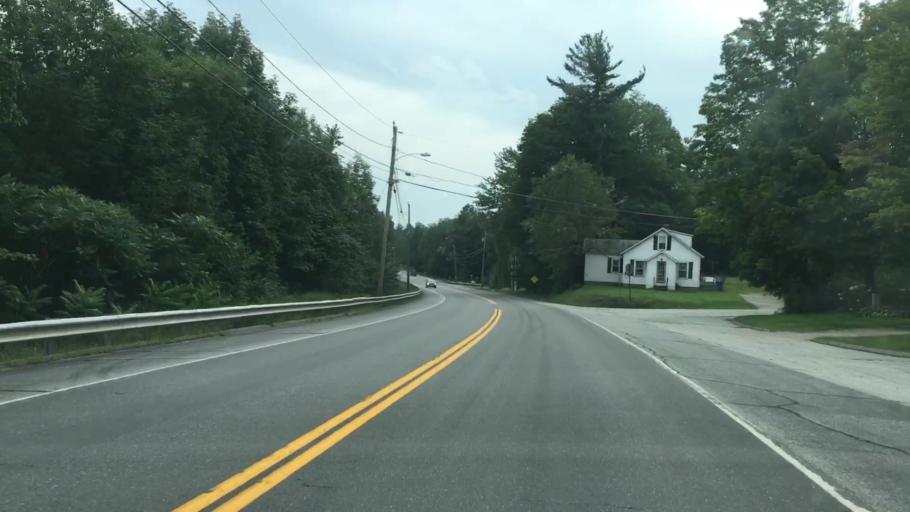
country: US
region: Maine
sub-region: Oxford County
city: Bethel
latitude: 44.4969
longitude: -70.6940
